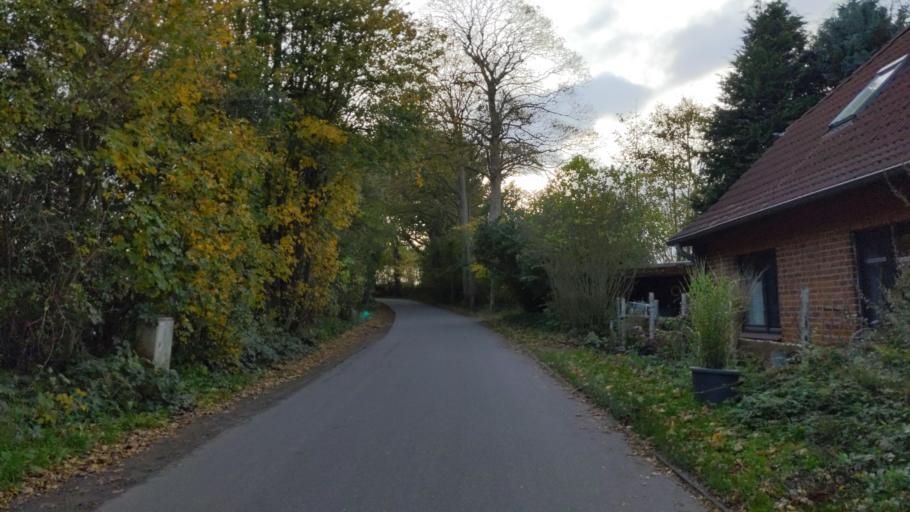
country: DE
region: Schleswig-Holstein
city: Susel
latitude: 54.0640
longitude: 10.7306
